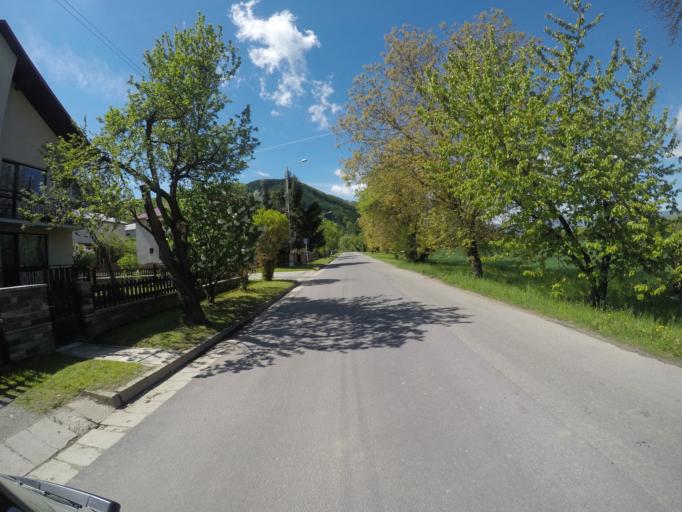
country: SK
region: Banskobystricky
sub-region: Okres Banska Bystrica
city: Banska Bystrica
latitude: 48.7359
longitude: 19.2042
